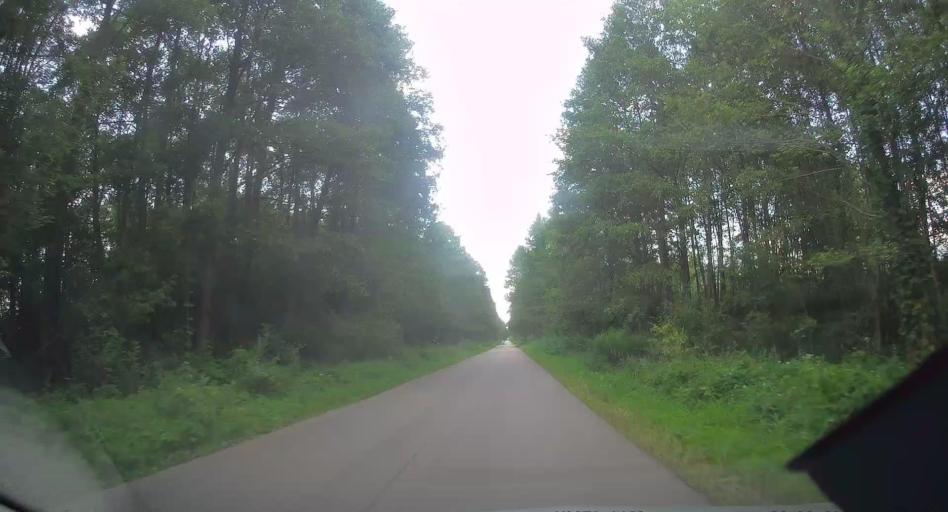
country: PL
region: Swietokrzyskie
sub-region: Powiat konecki
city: Ruda Maleniecka
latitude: 51.1348
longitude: 20.2423
